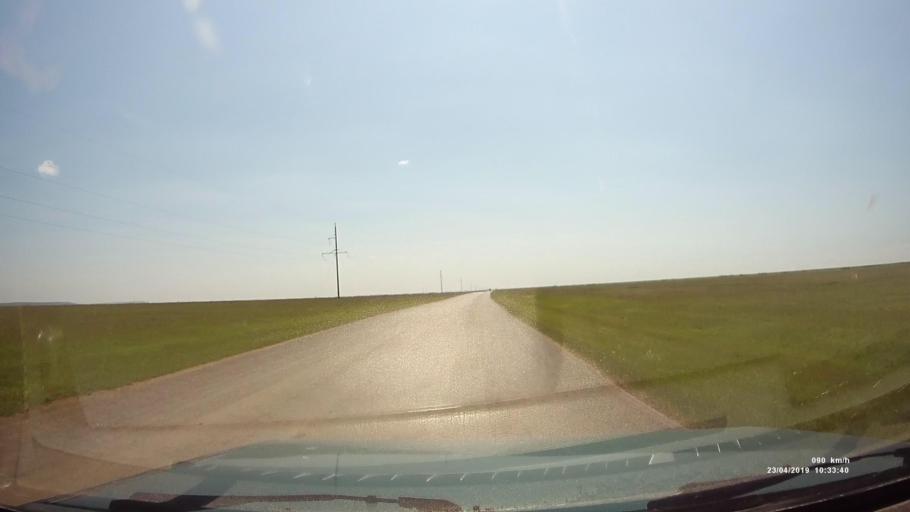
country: RU
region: Kalmykiya
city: Yashalta
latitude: 46.5714
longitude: 42.6002
